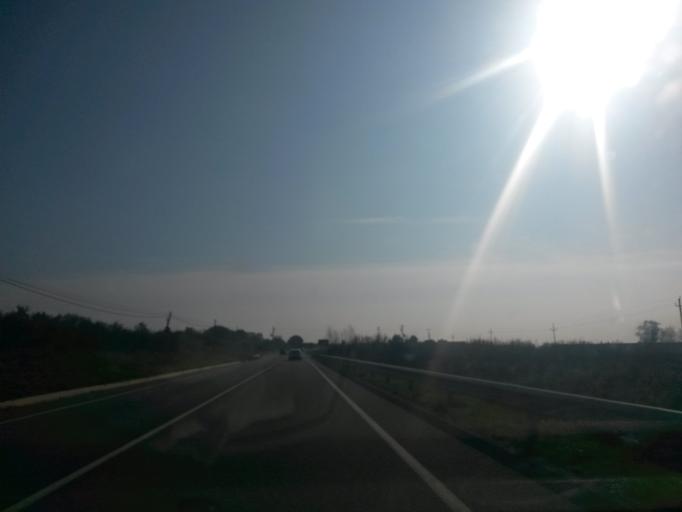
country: ES
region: Catalonia
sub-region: Provincia de Girona
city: Vilajuiga
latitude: 42.3297
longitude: 3.0869
